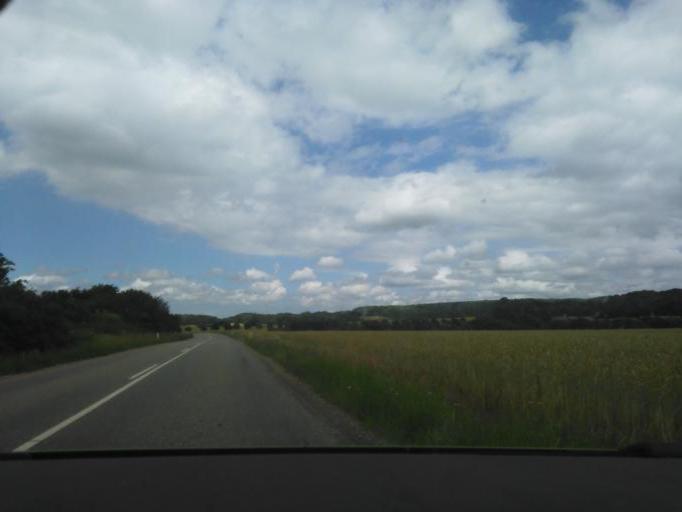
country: DK
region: Zealand
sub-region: Kalundborg Kommune
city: Hong
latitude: 55.5627
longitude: 11.3153
